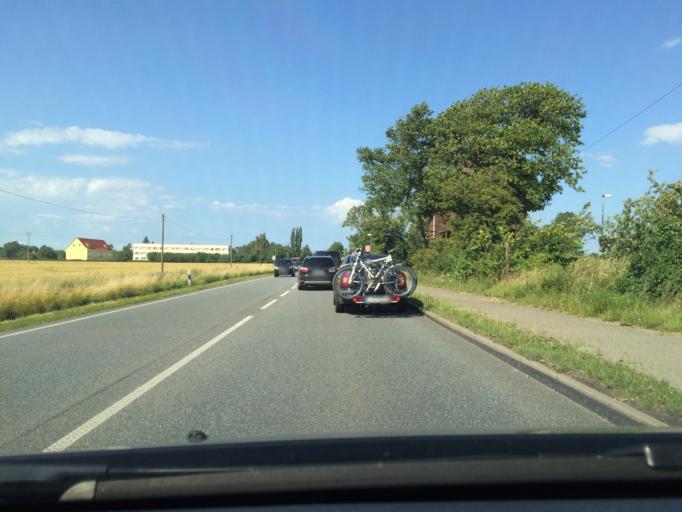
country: DE
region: Mecklenburg-Vorpommern
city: Monchhagen
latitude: 54.1431
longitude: 12.2245
